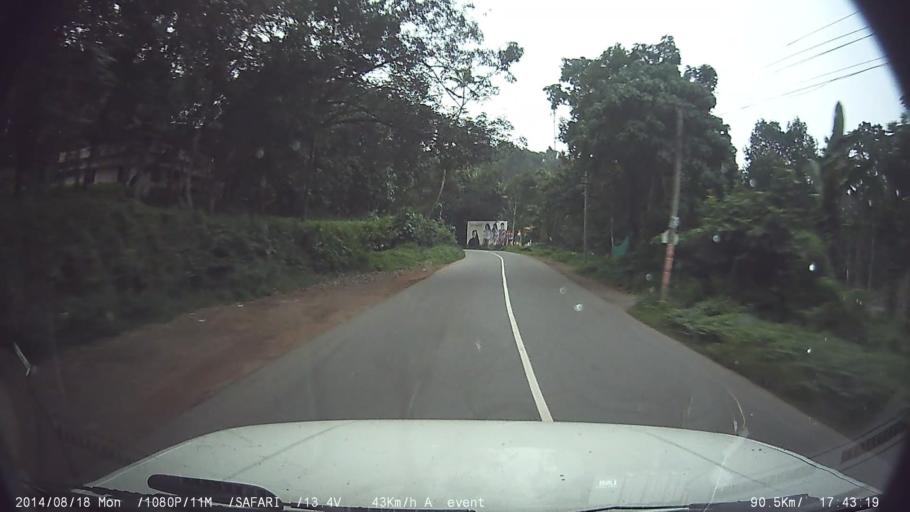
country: IN
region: Kerala
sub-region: Ernakulam
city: Muvattupuzha
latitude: 9.9362
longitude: 76.5763
